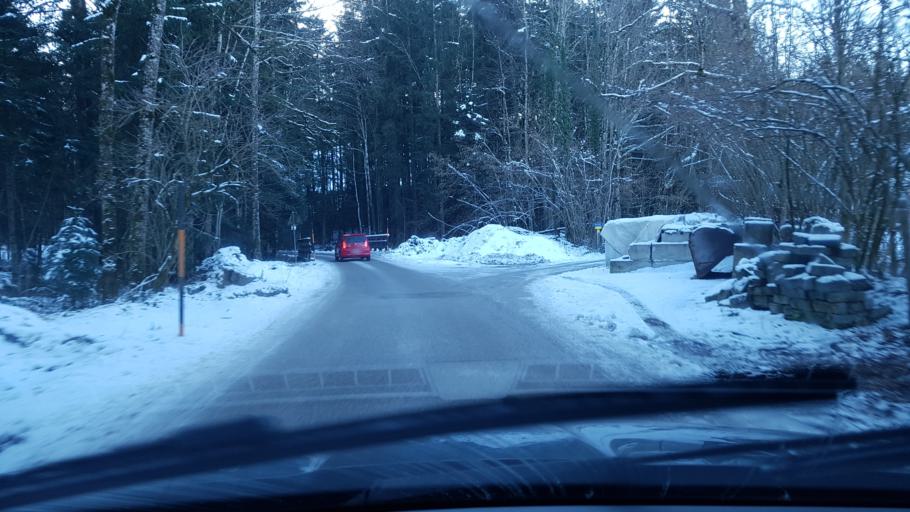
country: AT
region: Salzburg
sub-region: Politischer Bezirk Hallein
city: Scheffau am Tennengebirge
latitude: 47.6478
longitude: 13.2182
